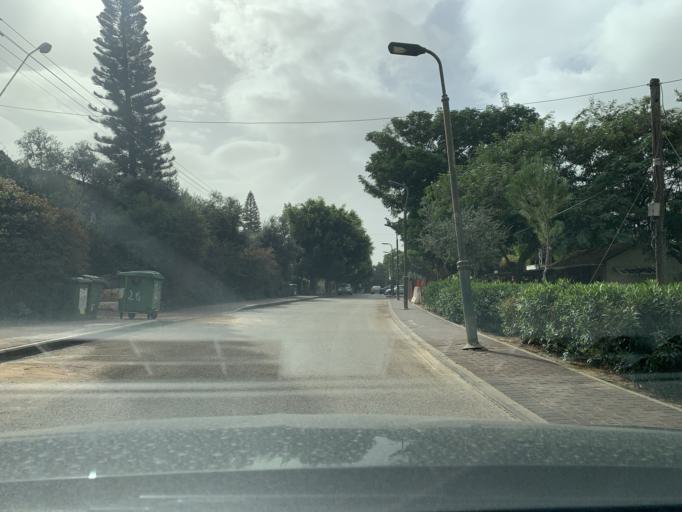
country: IL
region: Central District
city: Jaljulya
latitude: 32.1611
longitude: 34.9450
